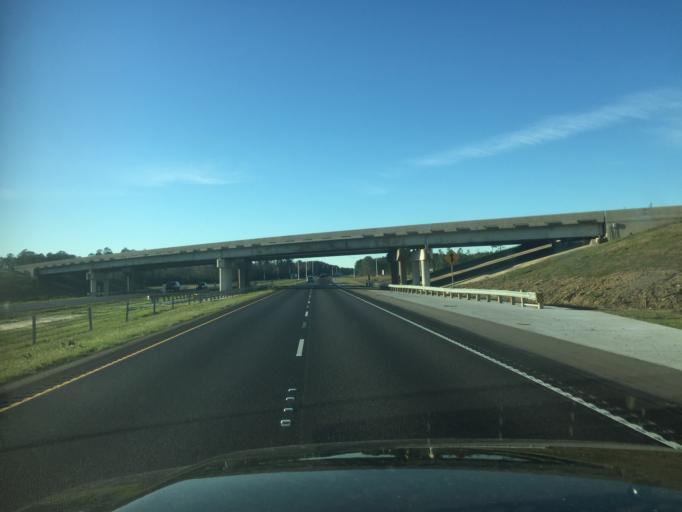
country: US
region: Louisiana
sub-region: Saint Tammany Parish
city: Mandeville
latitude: 30.3923
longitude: -90.0020
